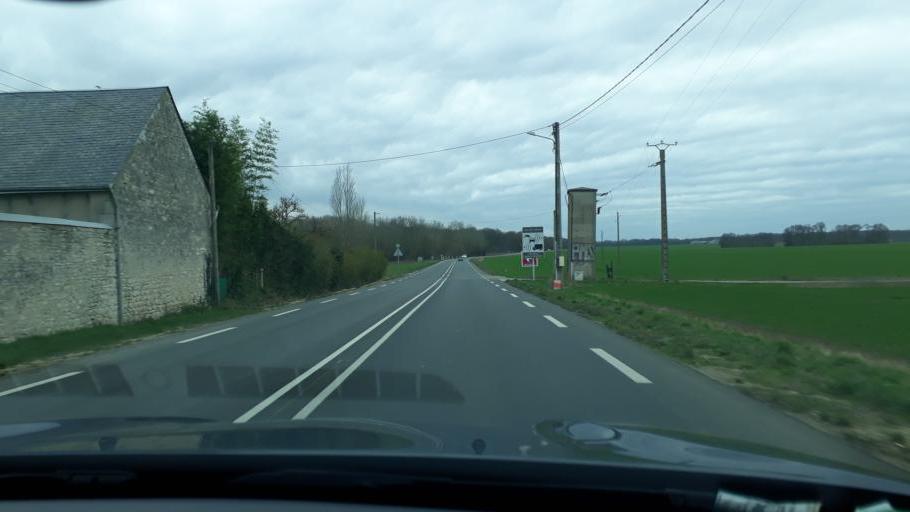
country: FR
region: Centre
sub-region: Departement du Loiret
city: Chanteau
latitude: 48.0291
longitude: 1.9721
